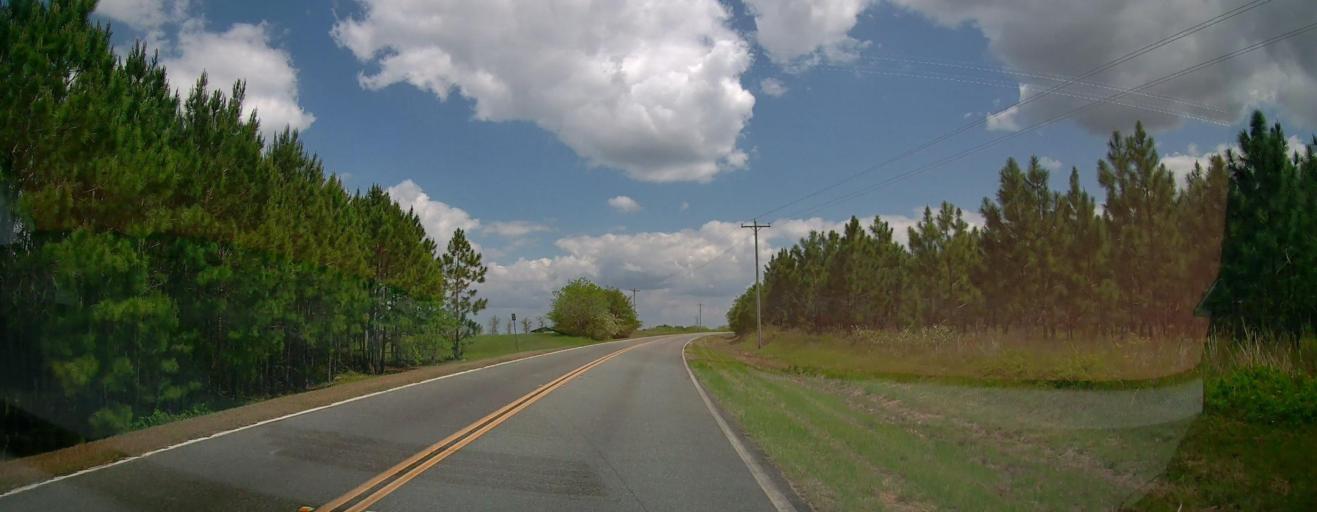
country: US
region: Georgia
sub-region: Laurens County
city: East Dublin
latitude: 32.5288
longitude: -82.6928
